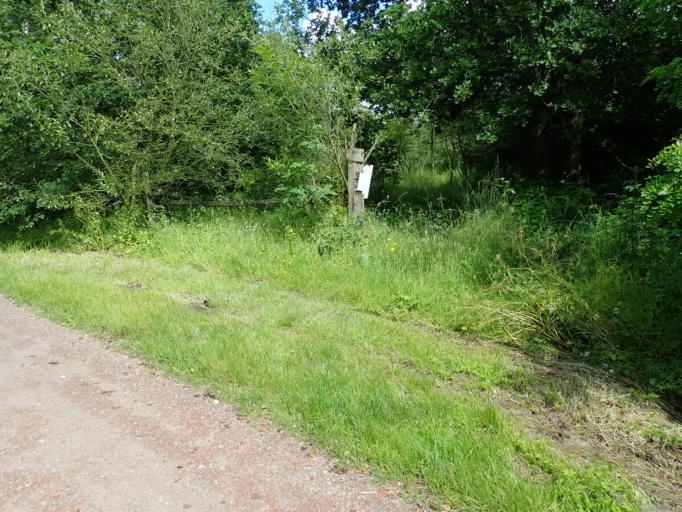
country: BE
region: Flanders
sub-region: Provincie Antwerpen
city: Heist-op-den-Berg
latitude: 51.0907
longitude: 4.7288
